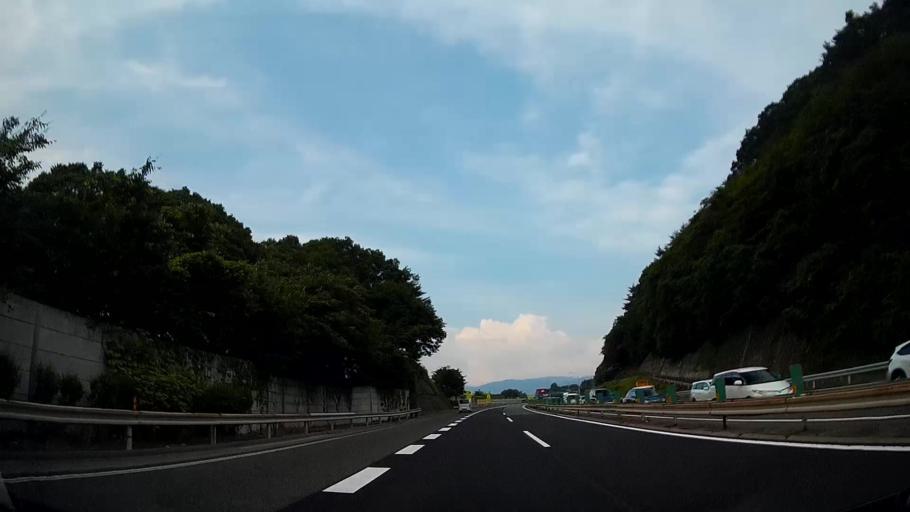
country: JP
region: Nagano
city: Okaya
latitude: 36.0504
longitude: 138.0365
